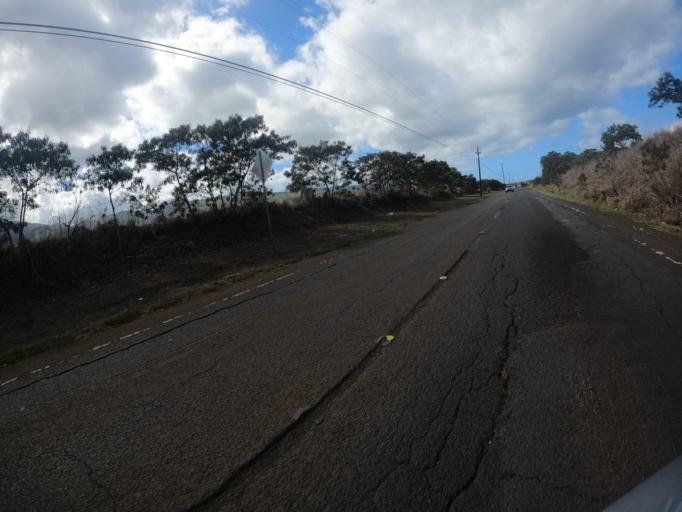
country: US
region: Hawaii
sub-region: Honolulu County
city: Waialua
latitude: 21.5703
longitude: -158.1389
